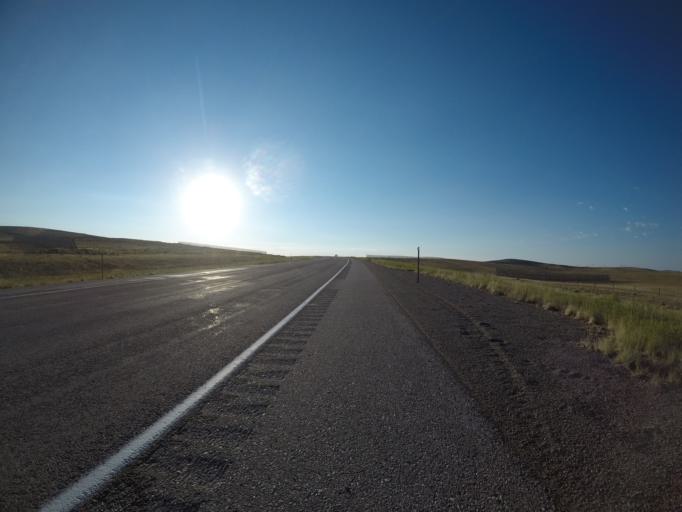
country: US
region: Wyoming
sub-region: Lincoln County
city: Kemmerer
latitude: 41.8680
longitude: -110.4674
